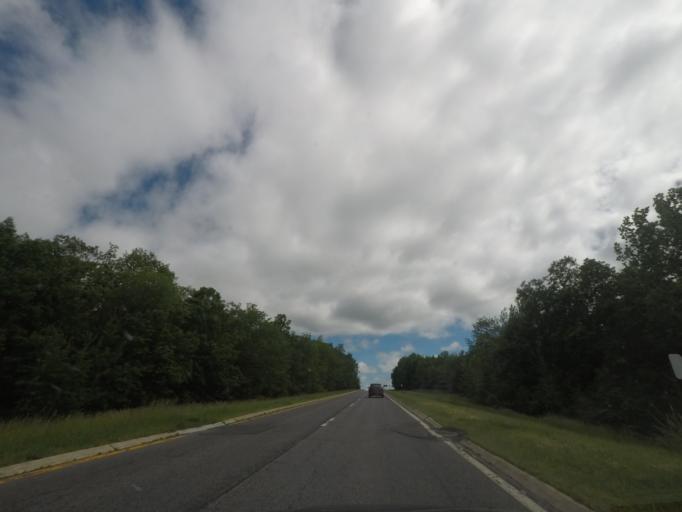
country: US
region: New York
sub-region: Columbia County
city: Philmont
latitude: 42.2666
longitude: -73.6144
